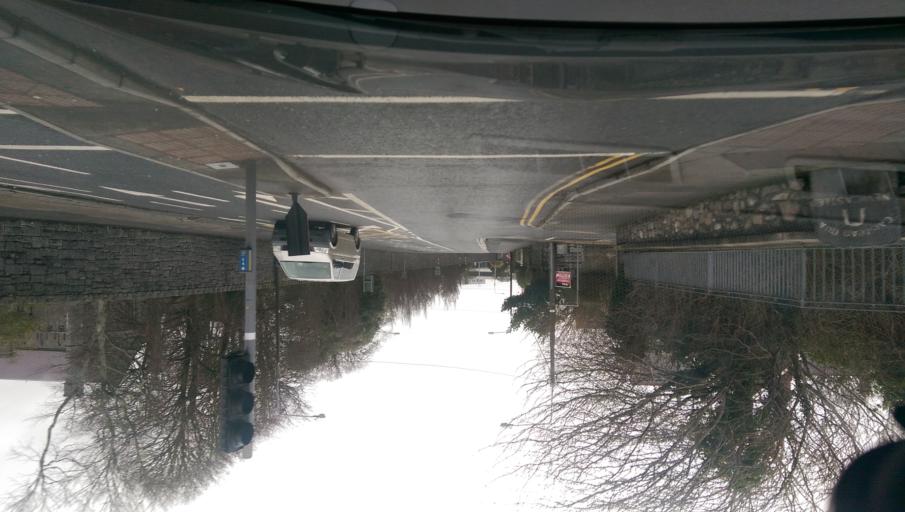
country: IE
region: Connaught
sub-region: County Galway
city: Gaillimh
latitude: 53.2772
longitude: -9.0636
